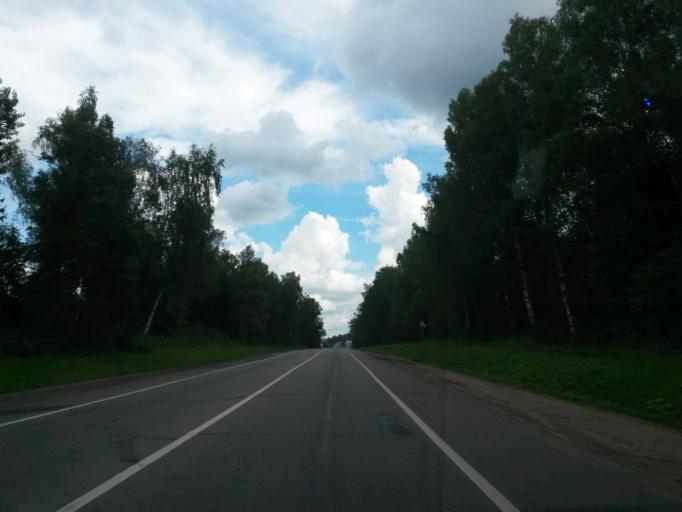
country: RU
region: Vladimir
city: Strunino
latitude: 56.5880
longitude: 38.6120
